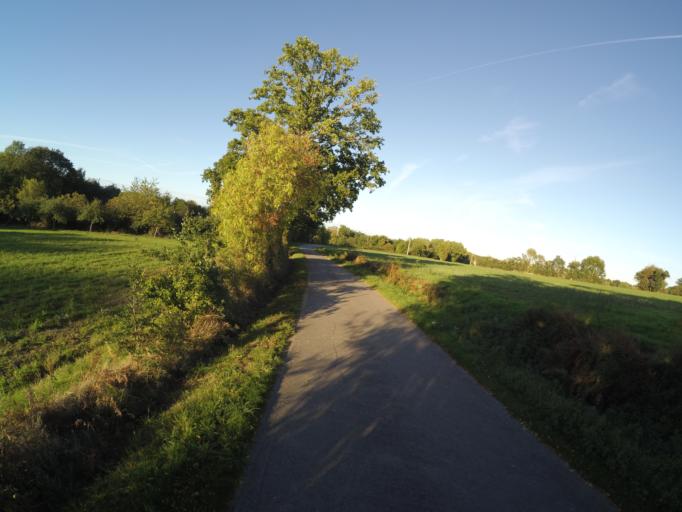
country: FR
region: Brittany
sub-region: Departement du Morbihan
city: Peillac
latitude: 47.7207
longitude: -2.2079
